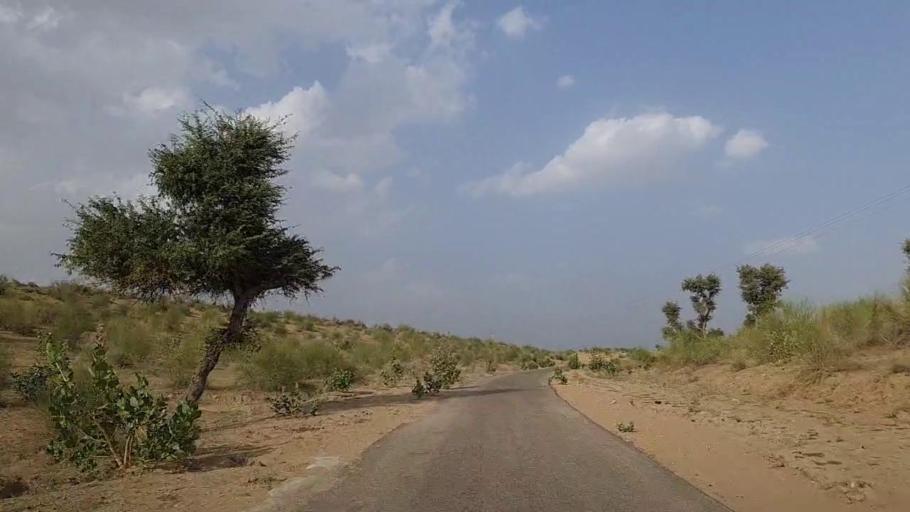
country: PK
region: Sindh
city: Islamkot
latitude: 24.7835
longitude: 70.1984
